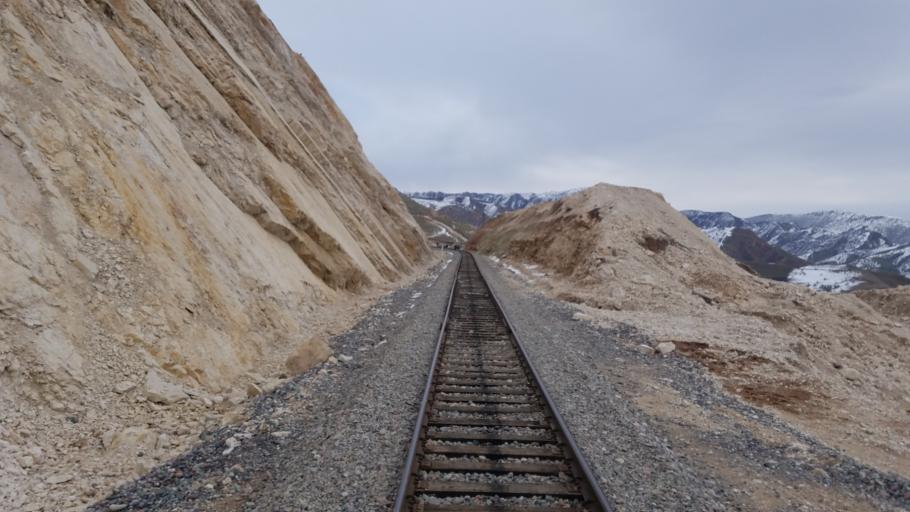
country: TJ
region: Khatlon
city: Yovon
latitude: 38.3909
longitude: 68.9574
